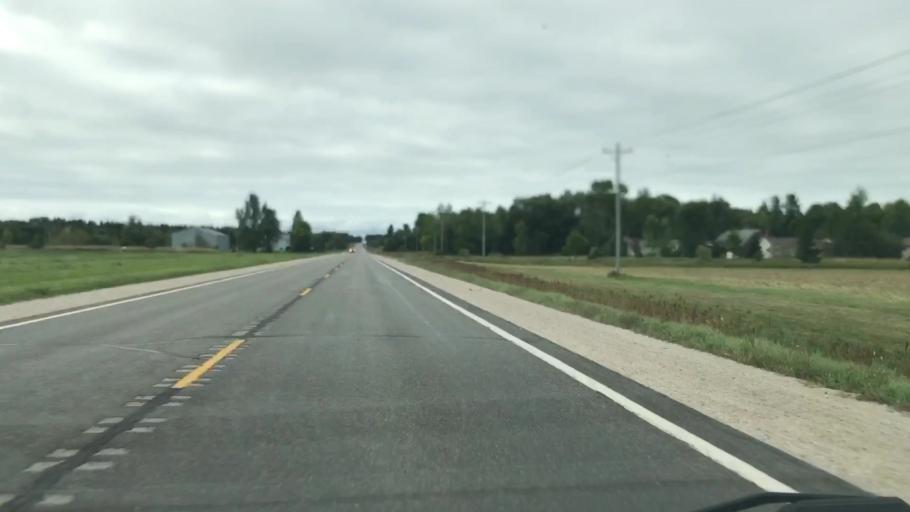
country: US
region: Michigan
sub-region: Luce County
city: Newberry
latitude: 46.1404
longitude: -85.5713
